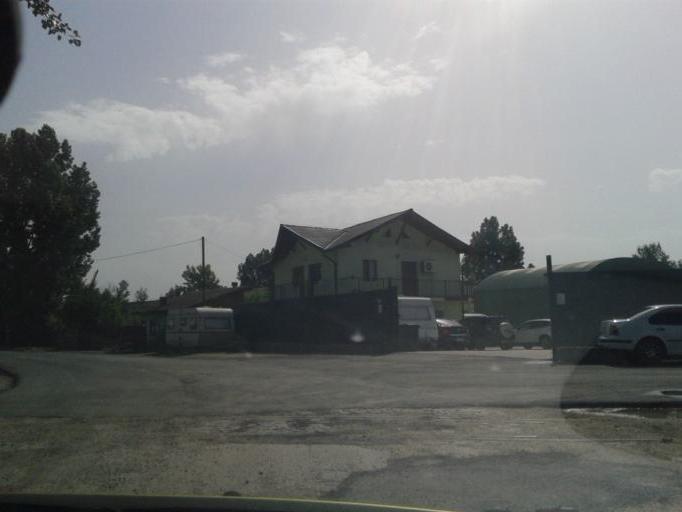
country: RO
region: Valcea
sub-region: Municipiul Ramnicu Valcea
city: Copacelu
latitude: 45.0663
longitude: 24.3341
